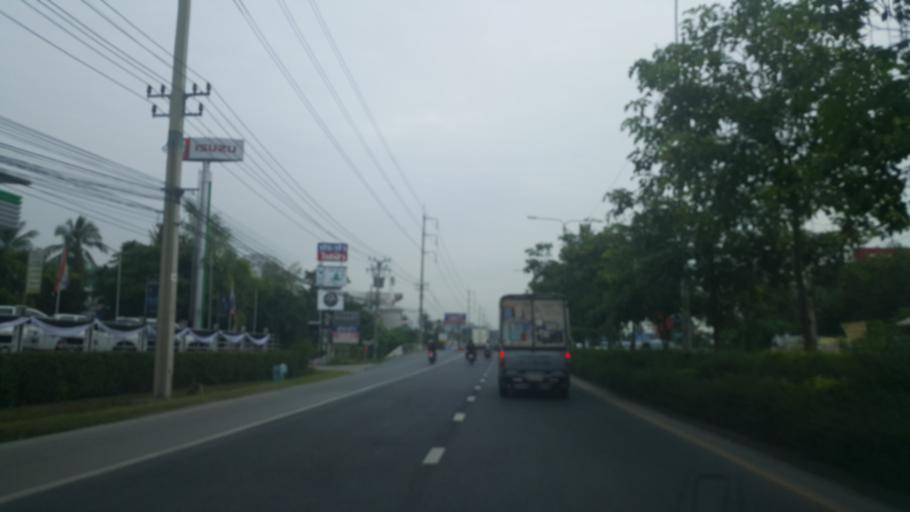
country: TH
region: Bangkok
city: Phasi Charoen
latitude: 13.7017
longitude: 100.4440
